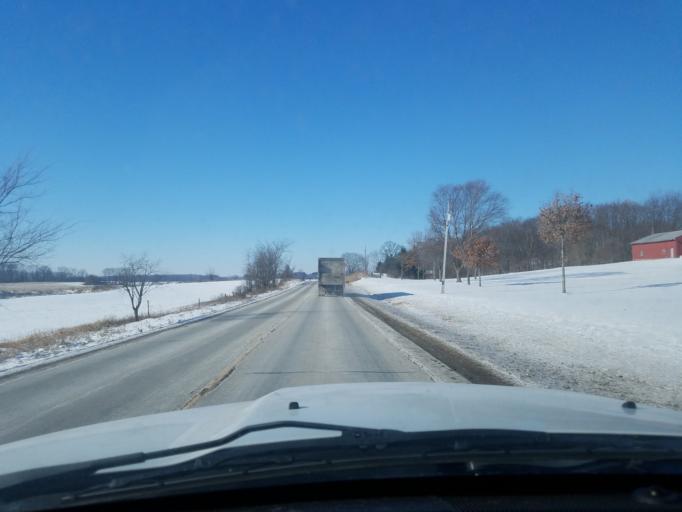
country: US
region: Indiana
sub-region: Noble County
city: Kendallville
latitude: 41.3954
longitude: -85.3352
